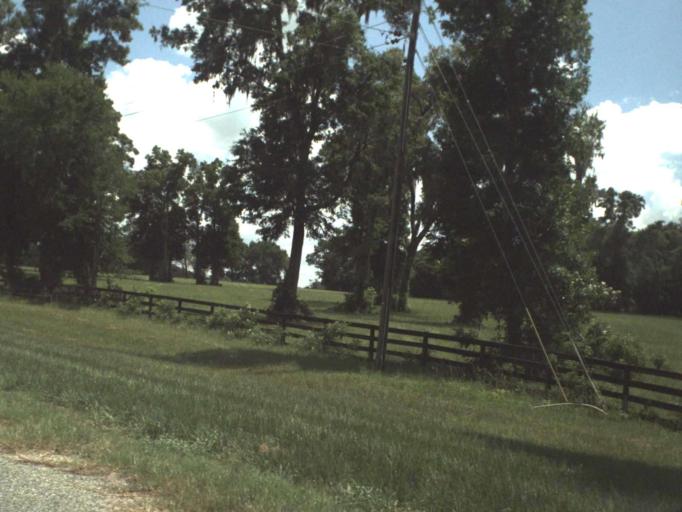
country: US
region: Florida
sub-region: Marion County
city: Citra
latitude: 29.3485
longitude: -82.1585
